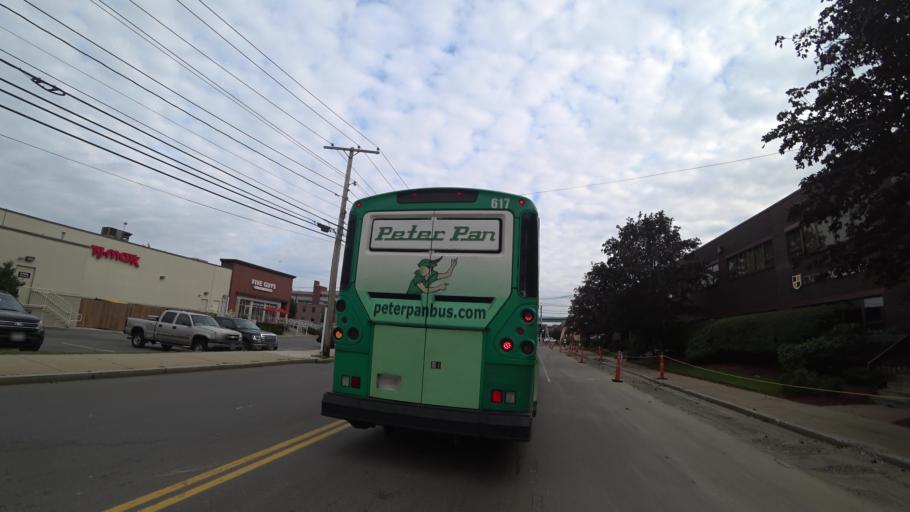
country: US
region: Massachusetts
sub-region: Suffolk County
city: Chelsea
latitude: 42.3939
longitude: -71.0435
